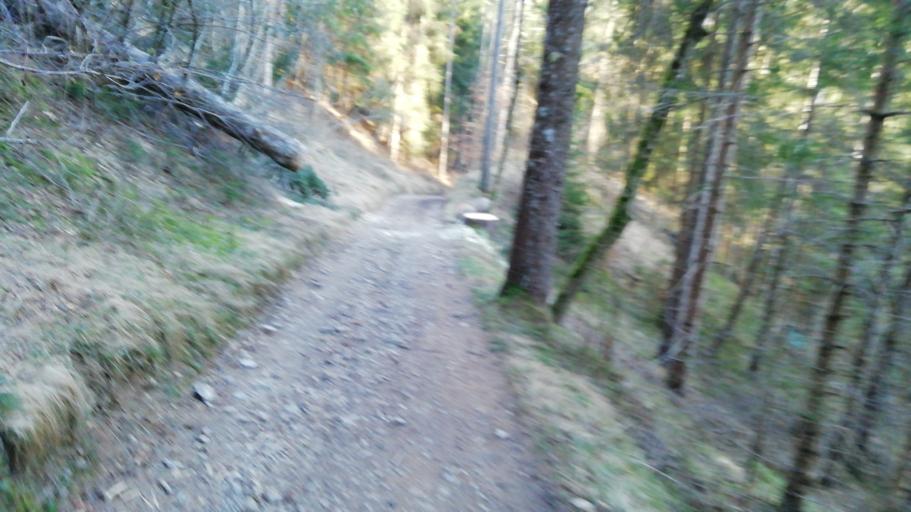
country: IT
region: Veneto
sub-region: Provincia di Belluno
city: Valle di Cadore
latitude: 46.4189
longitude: 12.3216
